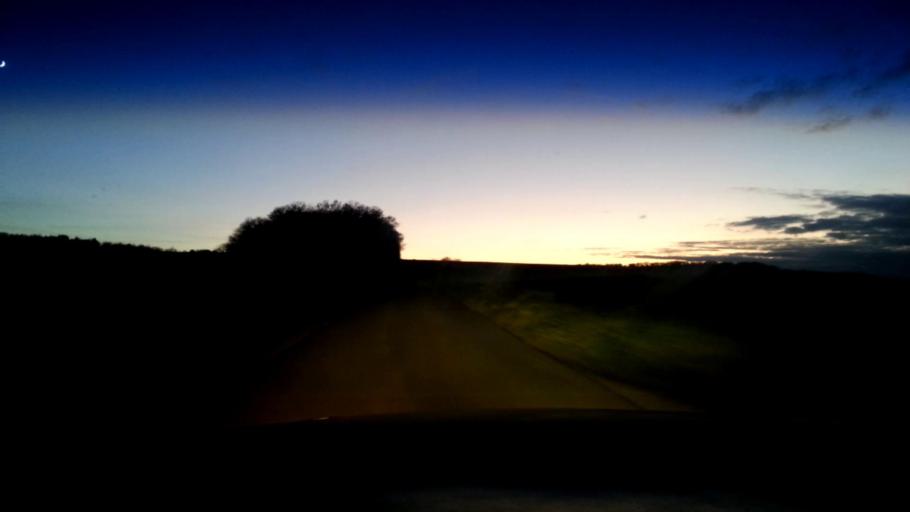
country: DE
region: Bavaria
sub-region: Upper Franconia
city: Litzendorf
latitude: 49.9399
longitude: 10.9915
